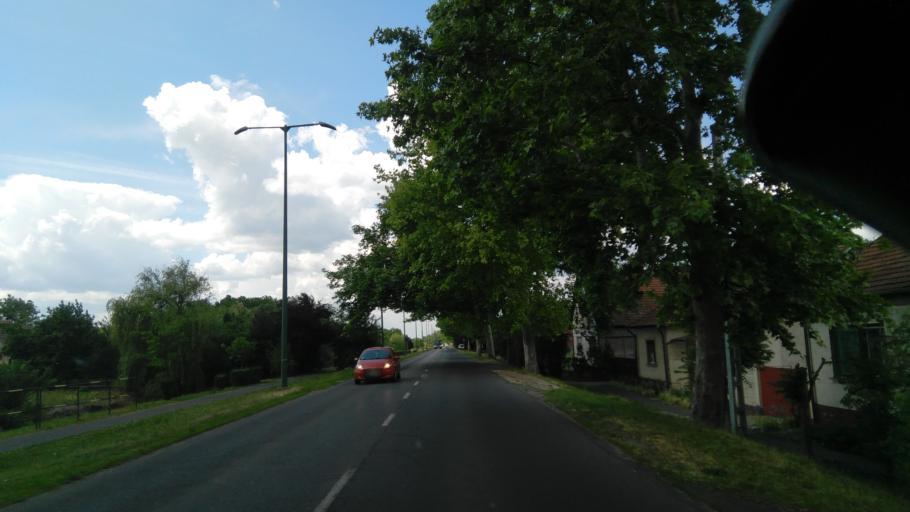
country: HU
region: Bekes
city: Gyula
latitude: 46.6471
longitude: 21.2525
